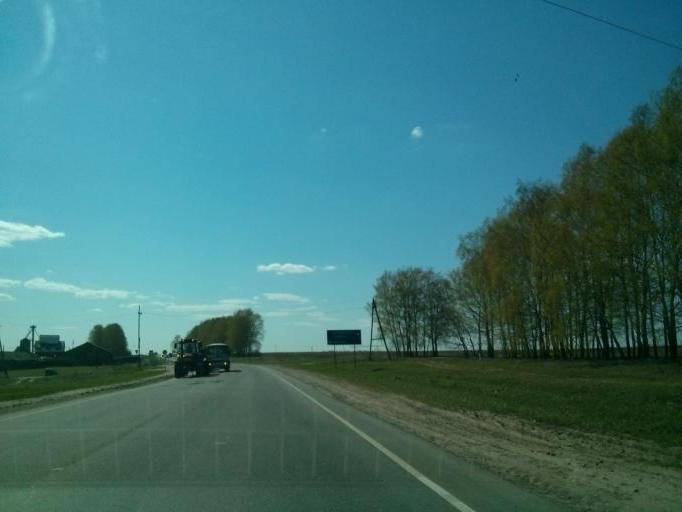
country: RU
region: Nizjnij Novgorod
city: Vorsma
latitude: 55.9645
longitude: 43.2069
